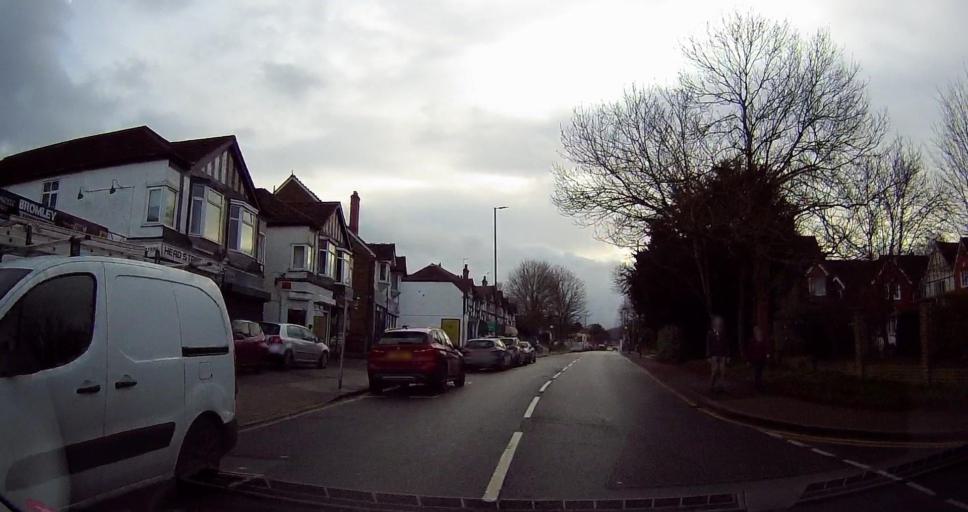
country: GB
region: England
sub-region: Greater London
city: Orpington
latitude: 51.3541
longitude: 0.0899
